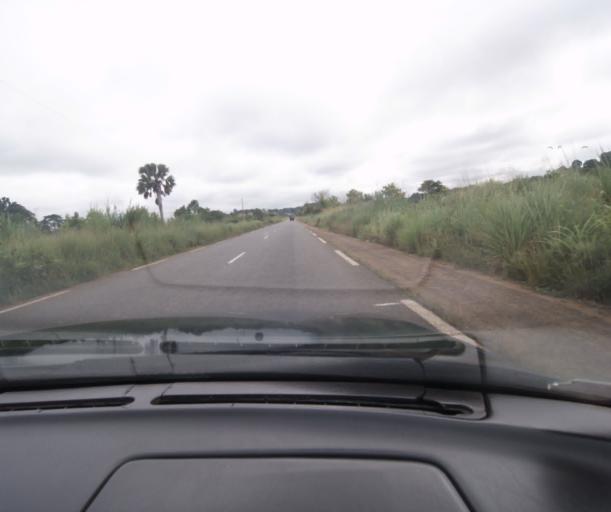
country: CM
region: Centre
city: Ombesa
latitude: 4.5613
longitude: 11.2633
